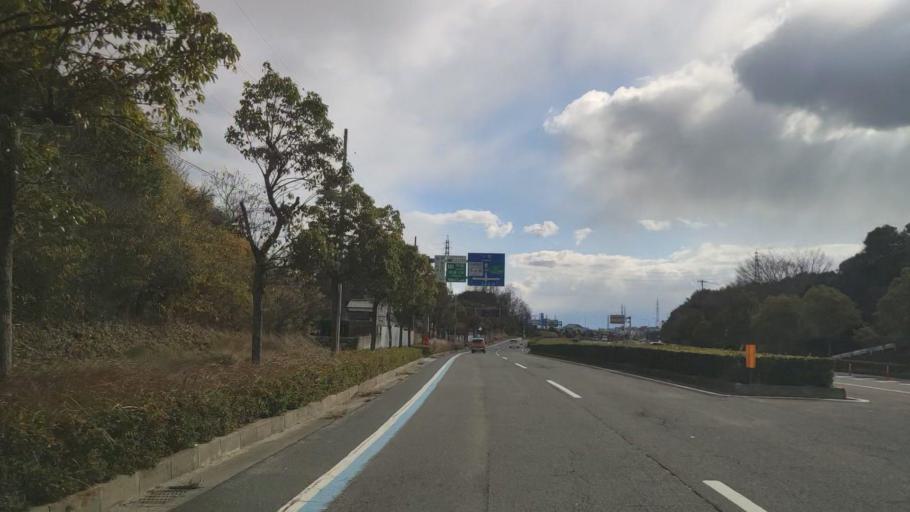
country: JP
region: Ehime
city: Hojo
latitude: 34.0572
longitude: 132.9736
